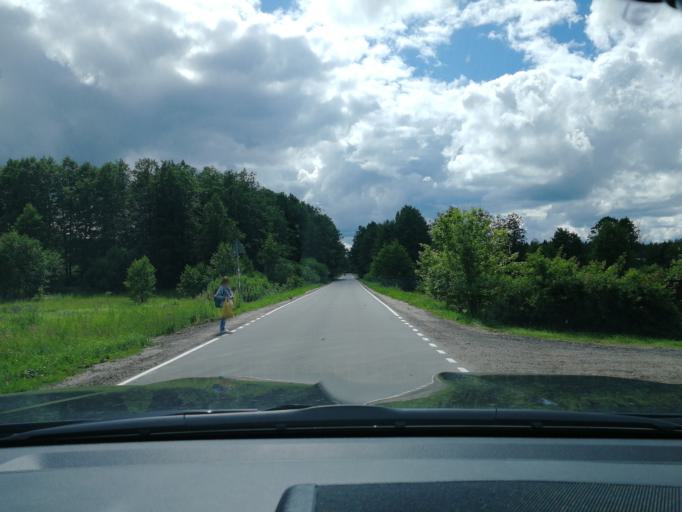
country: RU
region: Moskovskaya
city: Proletarskiy
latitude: 55.0114
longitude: 37.4796
